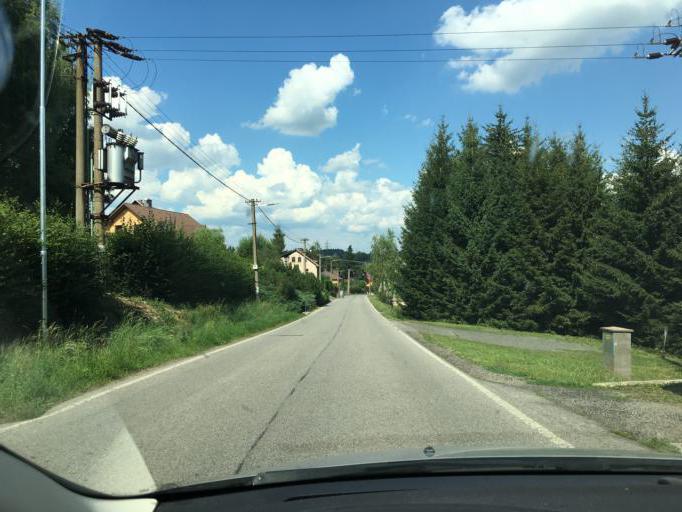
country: CZ
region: Liberecky
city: Semily
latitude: 50.6049
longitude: 15.3032
